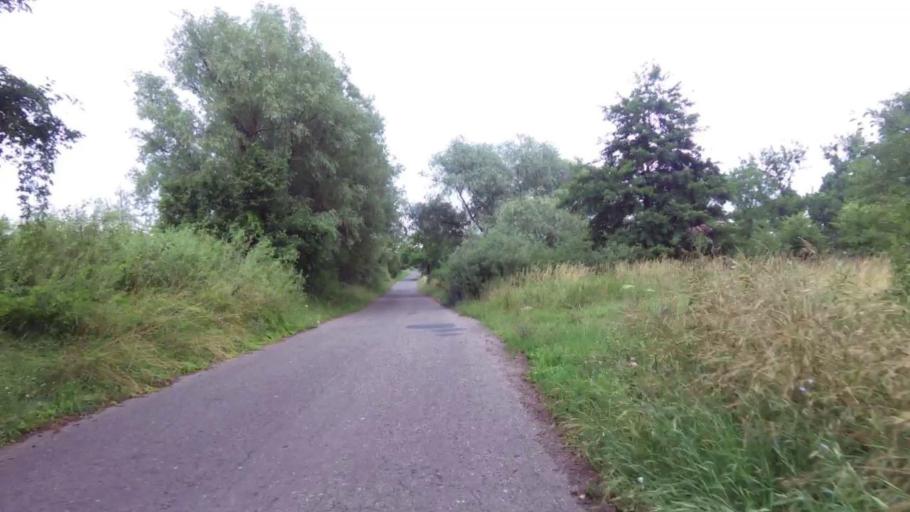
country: PL
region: West Pomeranian Voivodeship
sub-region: Powiat gryfinski
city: Moryn
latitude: 52.8700
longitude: 14.3329
